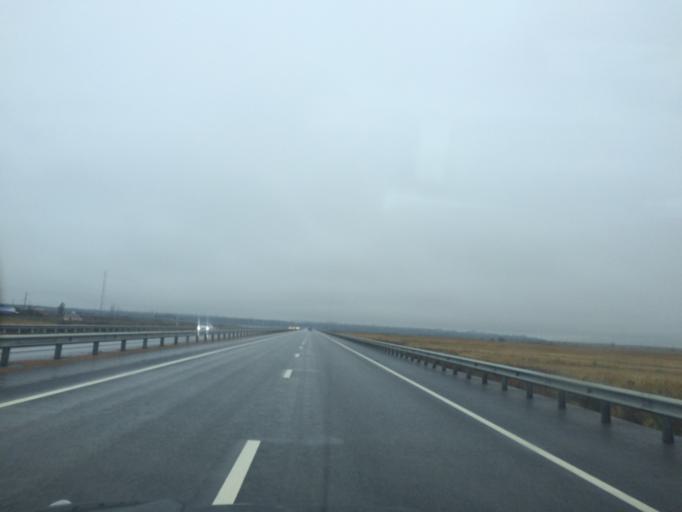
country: RU
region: Rostov
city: Kuleshovka
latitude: 47.0893
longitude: 39.5134
